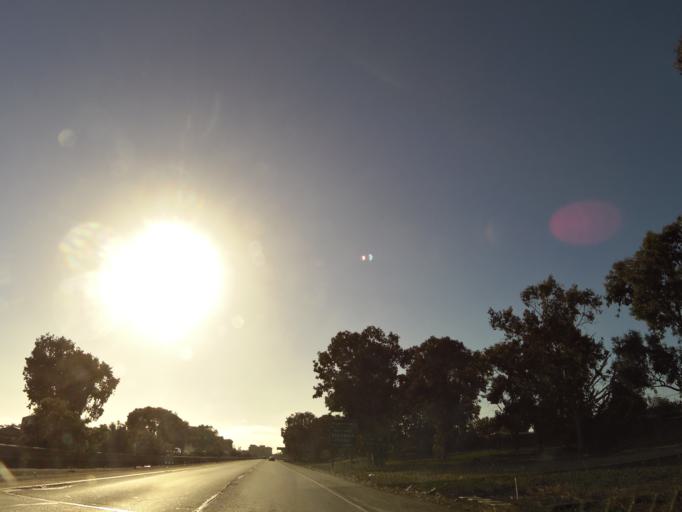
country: US
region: California
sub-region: Monterey County
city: Salinas
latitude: 36.6679
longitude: -121.6314
